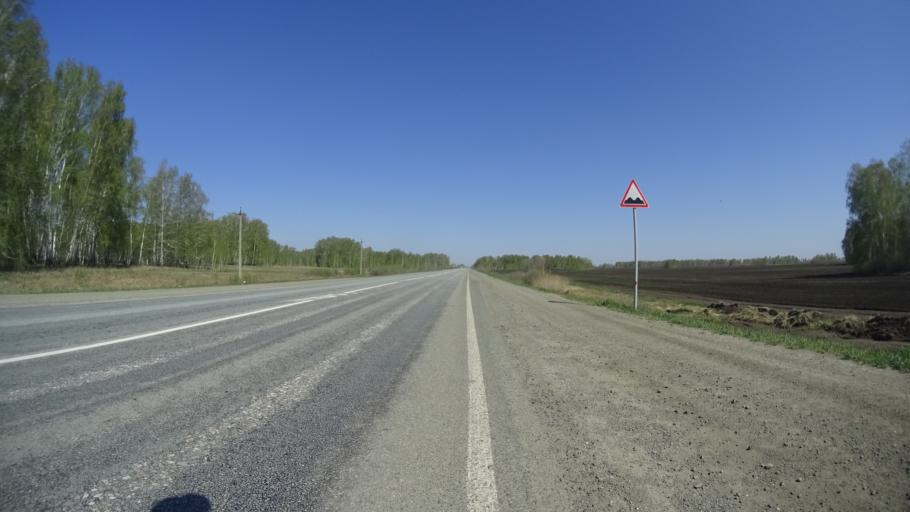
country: RU
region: Chelyabinsk
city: Troitsk
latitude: 54.1786
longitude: 61.4351
